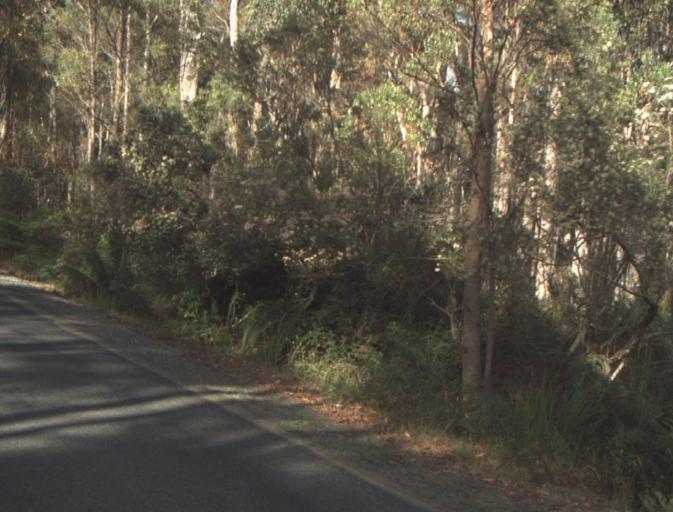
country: AU
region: Tasmania
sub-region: Dorset
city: Bridport
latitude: -41.1559
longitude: 147.2382
